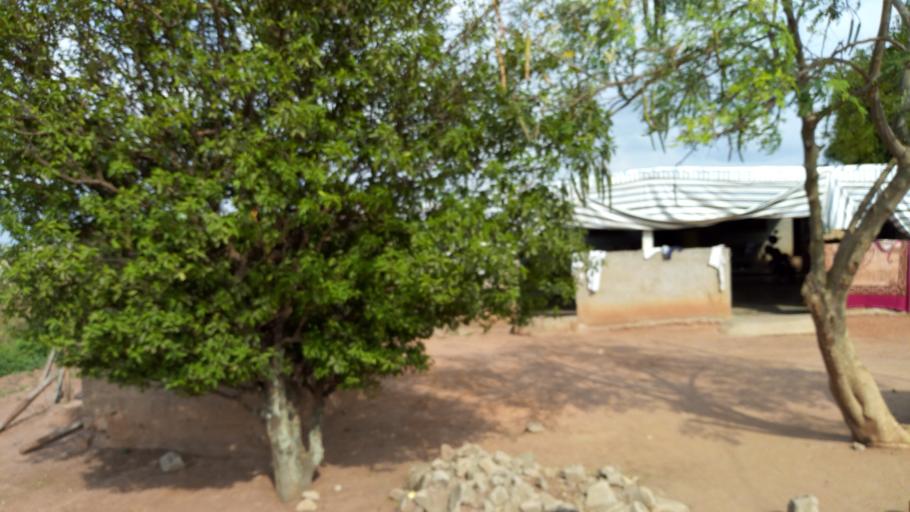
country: CI
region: Vallee du Bandama
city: Bouake
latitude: 7.7305
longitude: -5.0508
